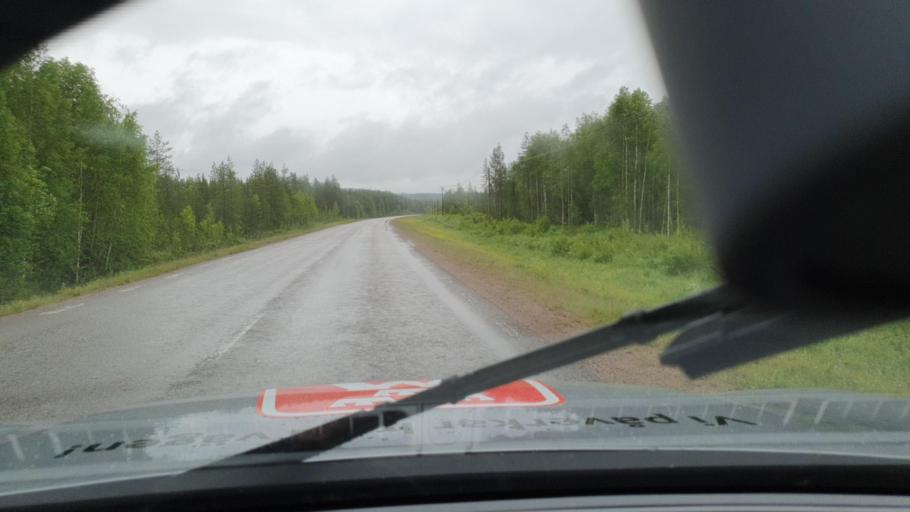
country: SE
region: Norrbotten
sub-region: Overkalix Kommun
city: OEverkalix
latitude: 66.4447
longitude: 23.1686
